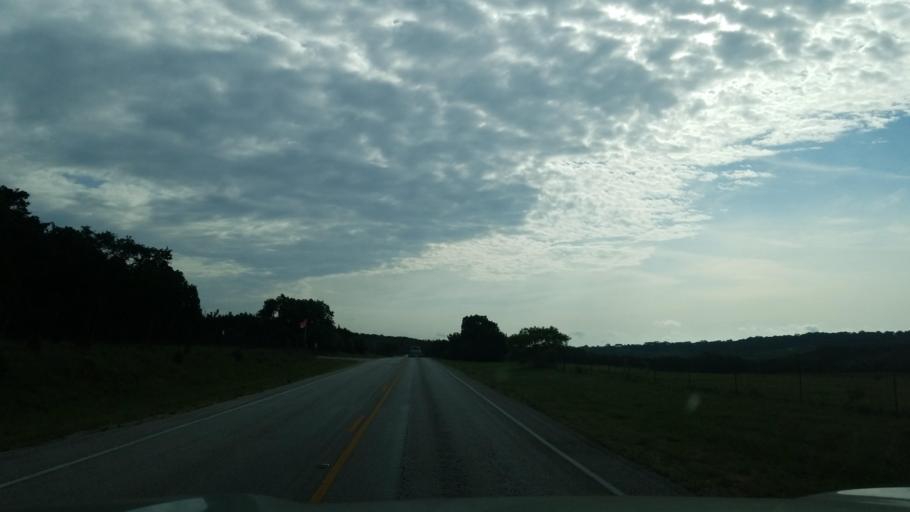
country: US
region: Texas
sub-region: Blanco County
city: Blanco
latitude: 30.1372
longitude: -98.2755
